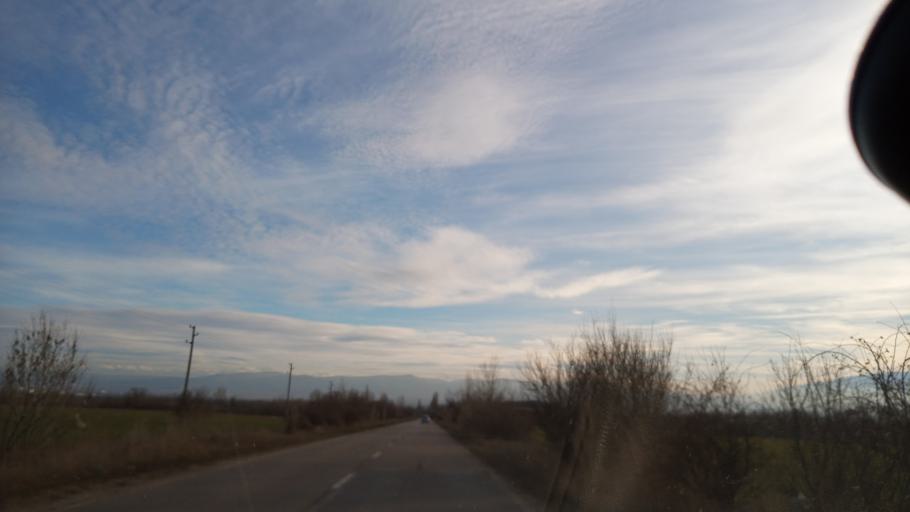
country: BG
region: Sofia-Capital
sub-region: Stolichna Obshtina
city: Bukhovo
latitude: 42.7448
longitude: 23.5560
